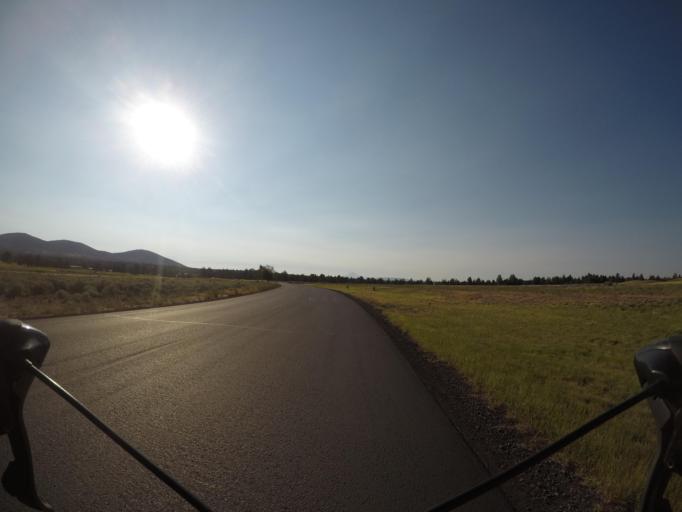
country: US
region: Oregon
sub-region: Deschutes County
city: Redmond
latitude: 44.2618
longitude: -121.2521
